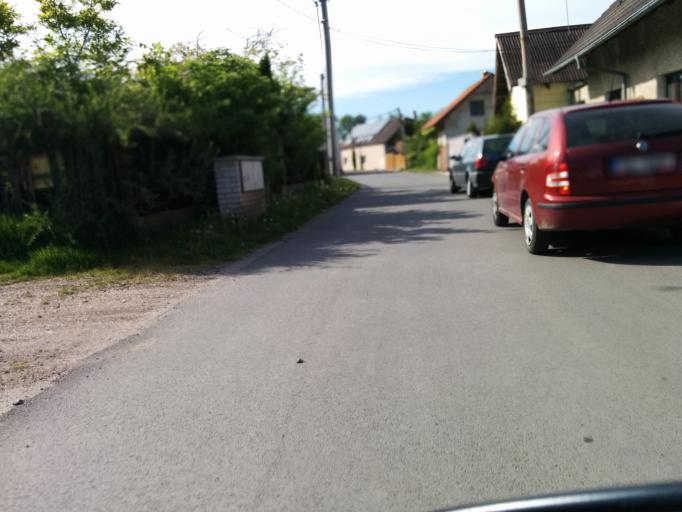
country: CZ
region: Central Bohemia
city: Libis
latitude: 50.2782
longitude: 14.5058
